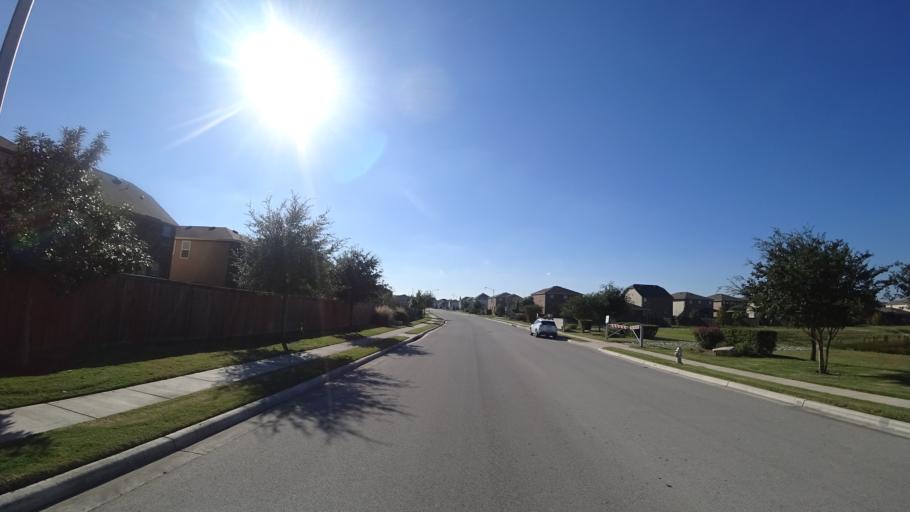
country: US
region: Texas
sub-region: Travis County
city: Manor
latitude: 30.3474
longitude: -97.6154
